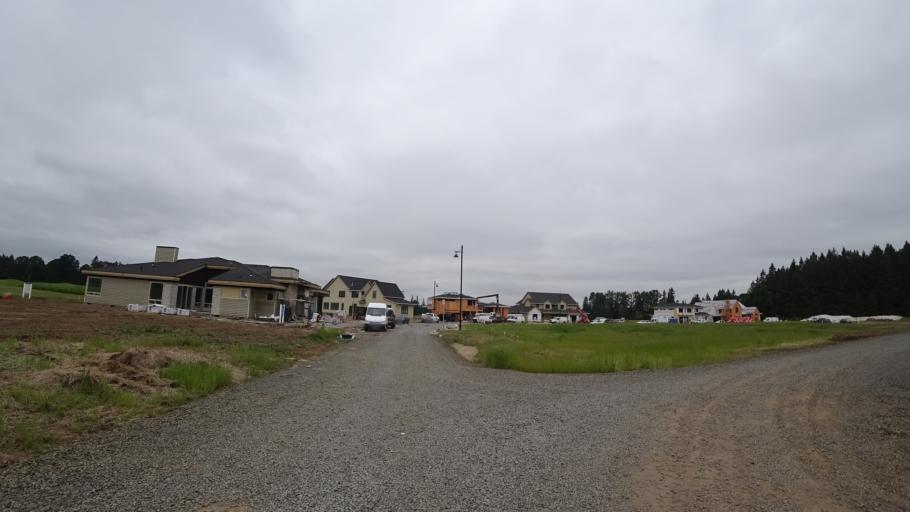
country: US
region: Oregon
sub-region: Washington County
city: Aloha
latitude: 45.4877
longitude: -122.9219
